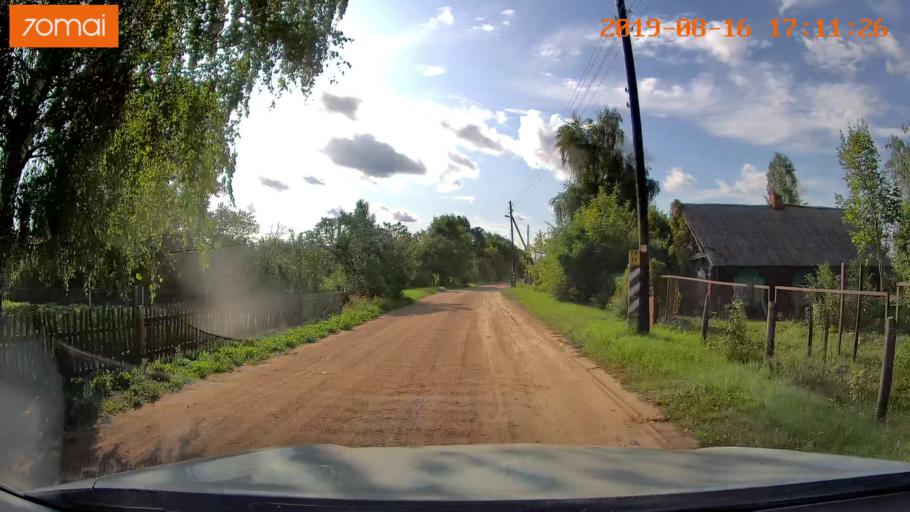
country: BY
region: Mogilev
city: Hlusha
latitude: 53.1956
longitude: 28.9062
